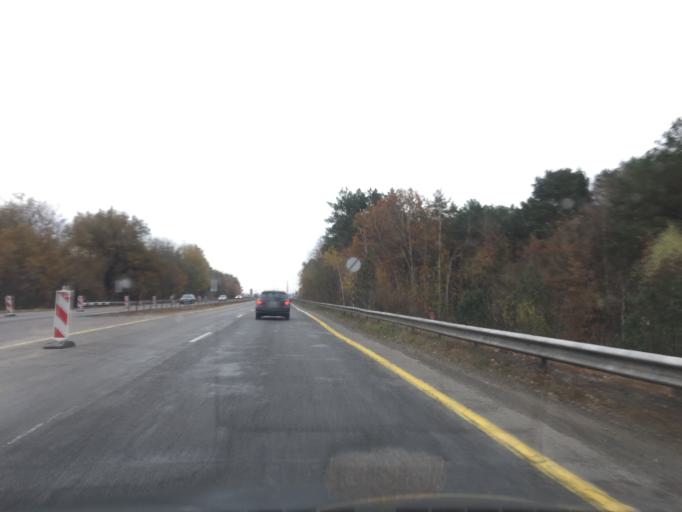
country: BY
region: Gomel
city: Horad Rechytsa
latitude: 52.3280
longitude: 30.5352
